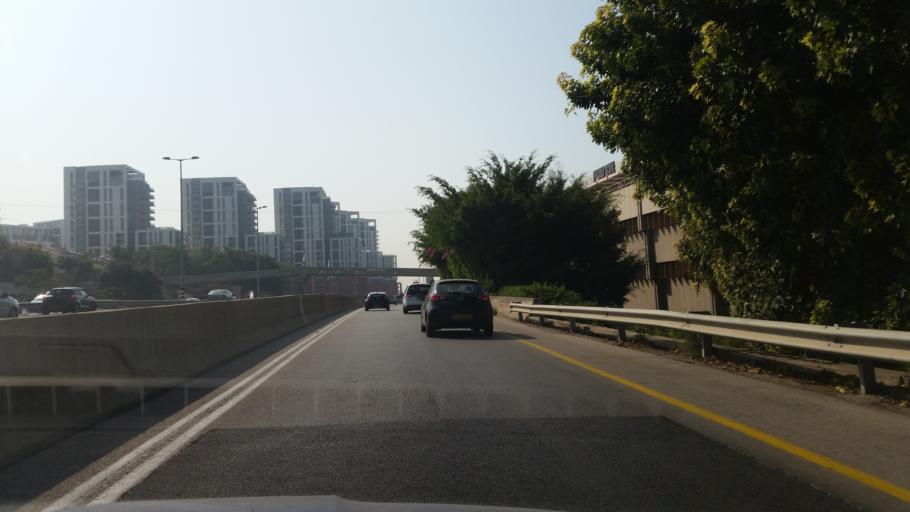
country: IL
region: Tel Aviv
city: Herzliyya
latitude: 32.1661
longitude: 34.8138
